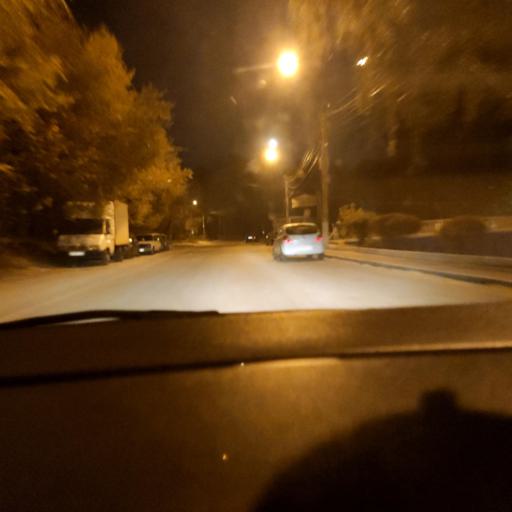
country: RU
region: Voronezj
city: Podgornoye
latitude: 51.6889
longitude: 39.1370
